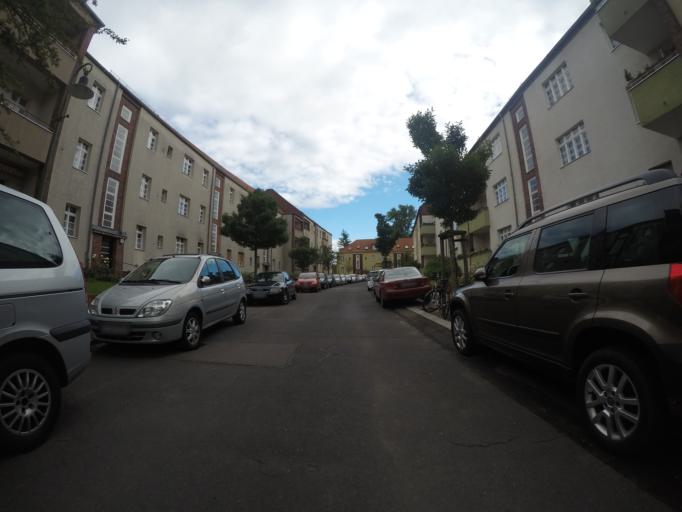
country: DE
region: Berlin
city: Schmargendorf
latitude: 52.4717
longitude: 13.2951
